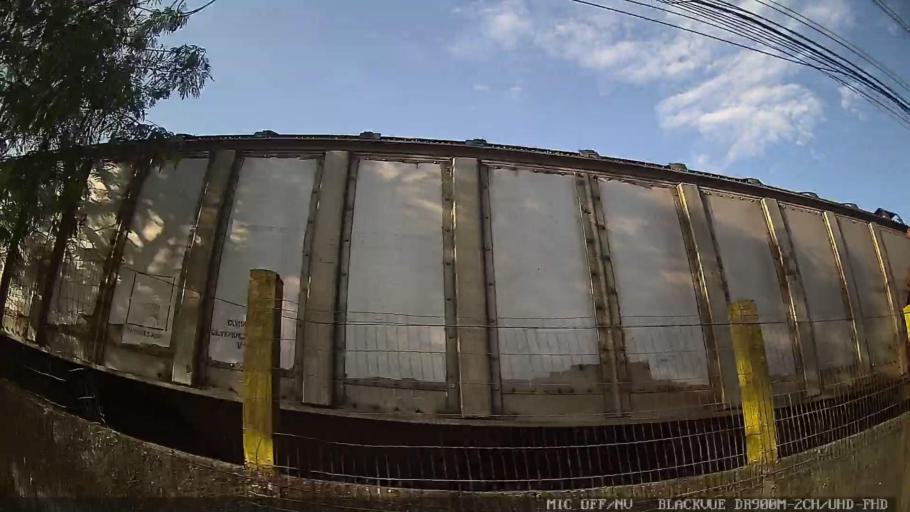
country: BR
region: Sao Paulo
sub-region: Cubatao
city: Cubatao
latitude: -23.9112
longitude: -46.4218
